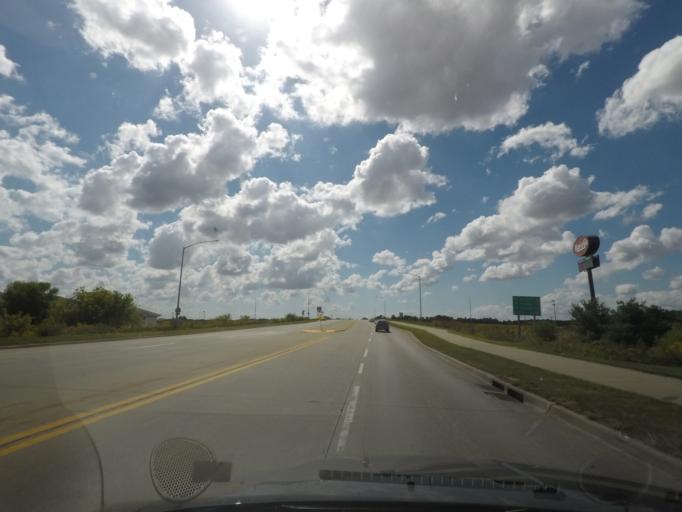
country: US
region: Iowa
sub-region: Story County
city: Ames
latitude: 42.0112
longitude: -93.6787
